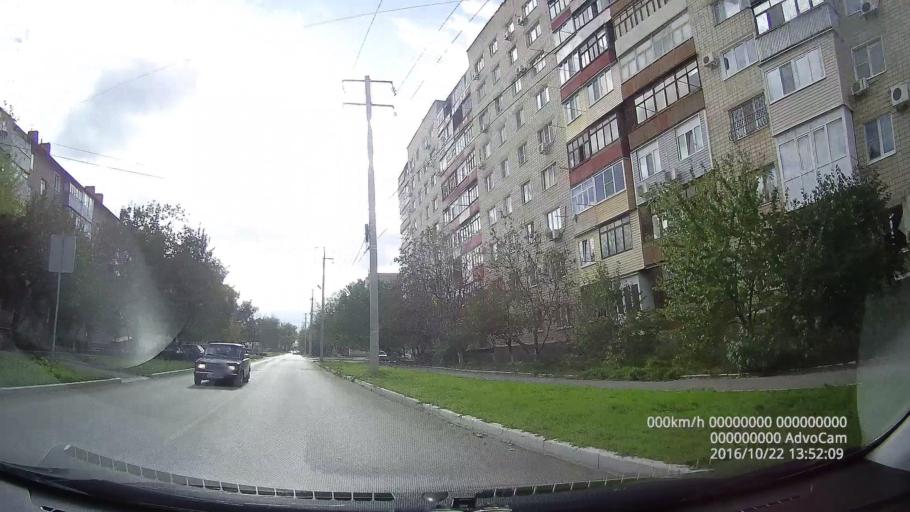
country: RU
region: Rostov
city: Kamensk-Shakhtinskiy
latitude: 48.3147
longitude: 40.2603
